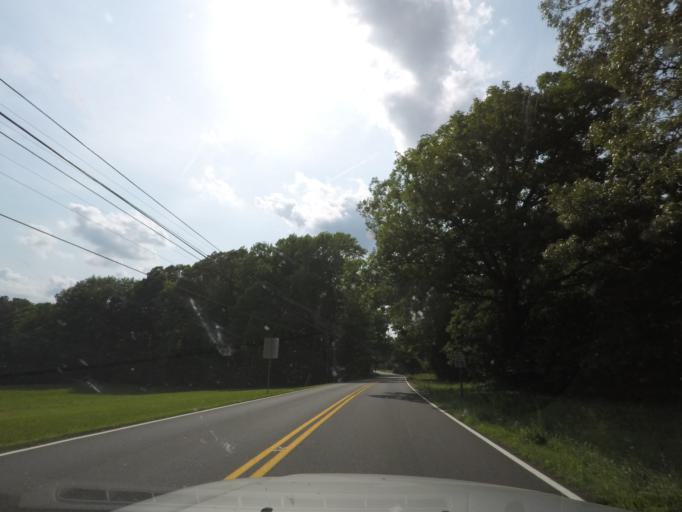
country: US
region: Virginia
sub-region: Fluvanna County
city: Weber City
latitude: 37.7549
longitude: -78.2740
